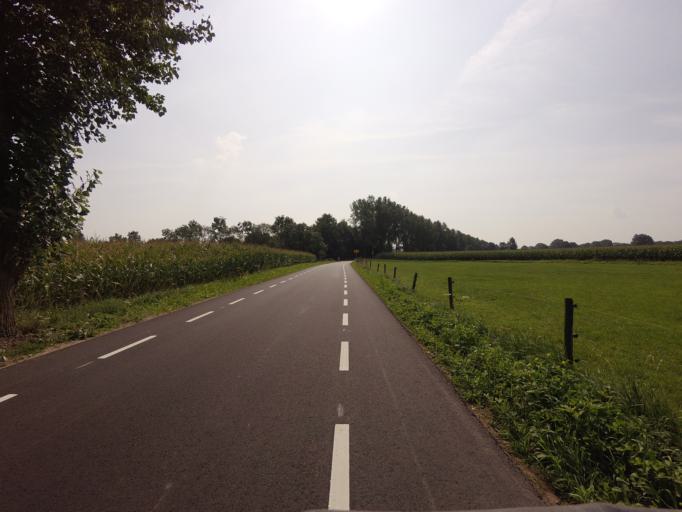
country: NL
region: Gelderland
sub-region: Gemeente Zevenaar
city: Zevenaar
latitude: 51.9131
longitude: 6.1351
